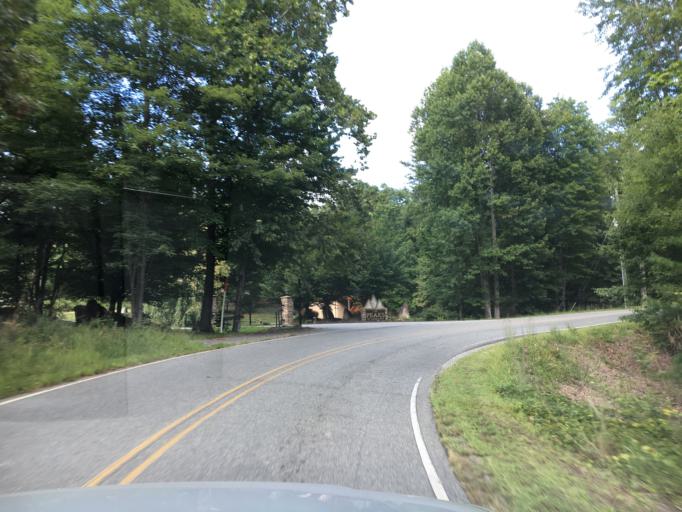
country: US
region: North Carolina
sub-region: Rutherford County
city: Lake Lure
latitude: 35.4015
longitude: -82.1820
